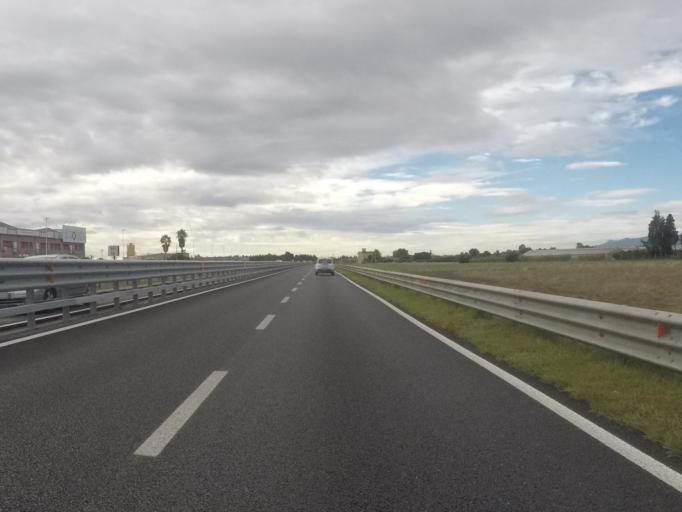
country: IT
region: Sardinia
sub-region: Provincia di Cagliari
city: Decimomannu
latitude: 39.3127
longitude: 8.9812
